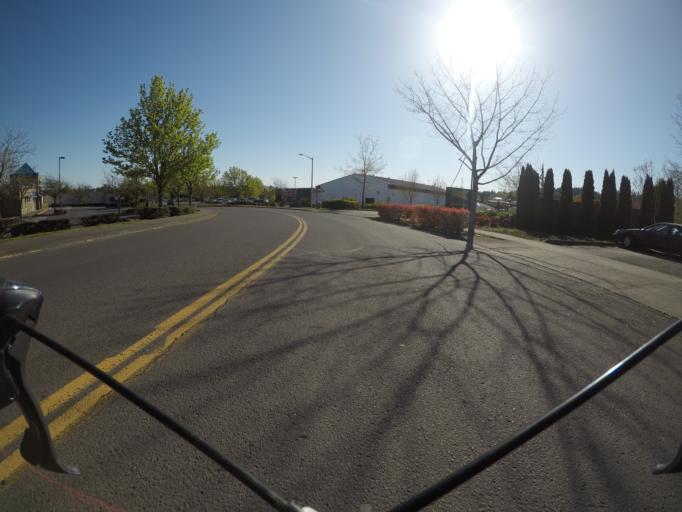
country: US
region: Oregon
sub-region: Washington County
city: King City
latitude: 45.4091
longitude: -122.7928
